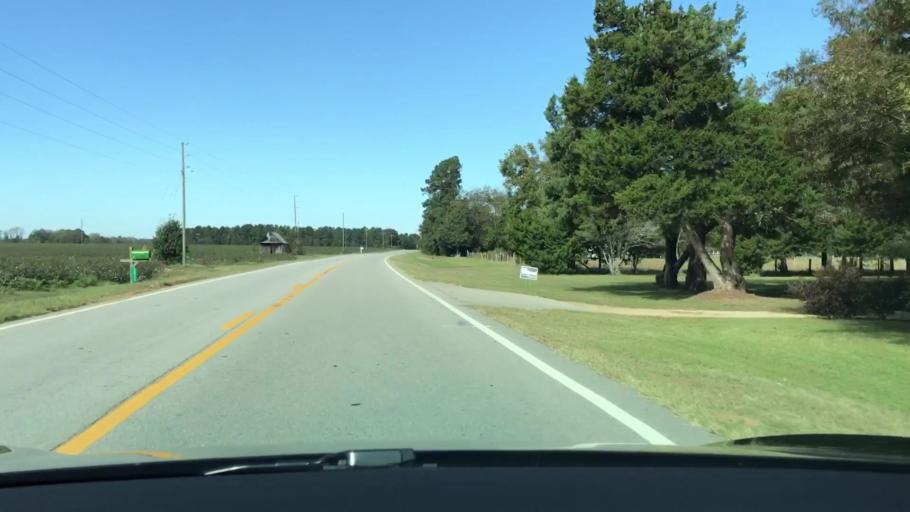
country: US
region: Georgia
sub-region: Glascock County
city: Gibson
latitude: 33.3108
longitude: -82.5376
